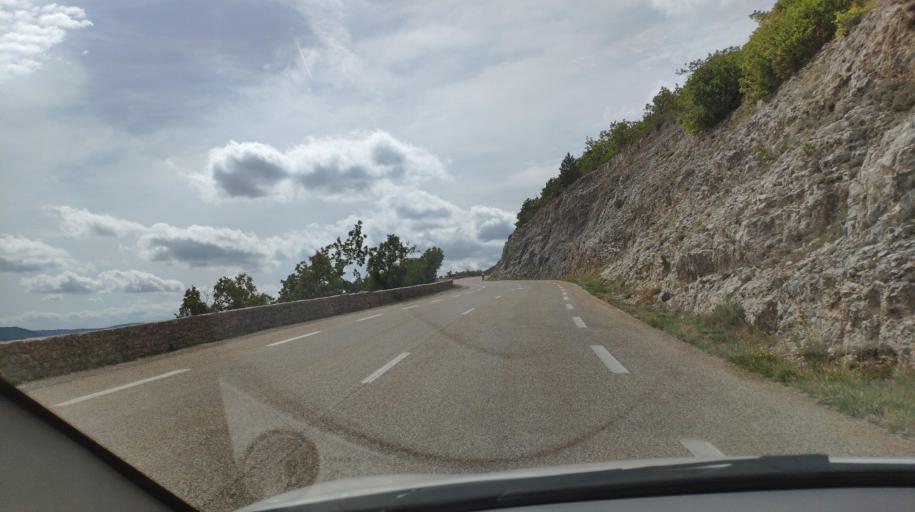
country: FR
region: Provence-Alpes-Cote d'Azur
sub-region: Departement du Vaucluse
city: Sault
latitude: 44.0737
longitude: 5.3583
